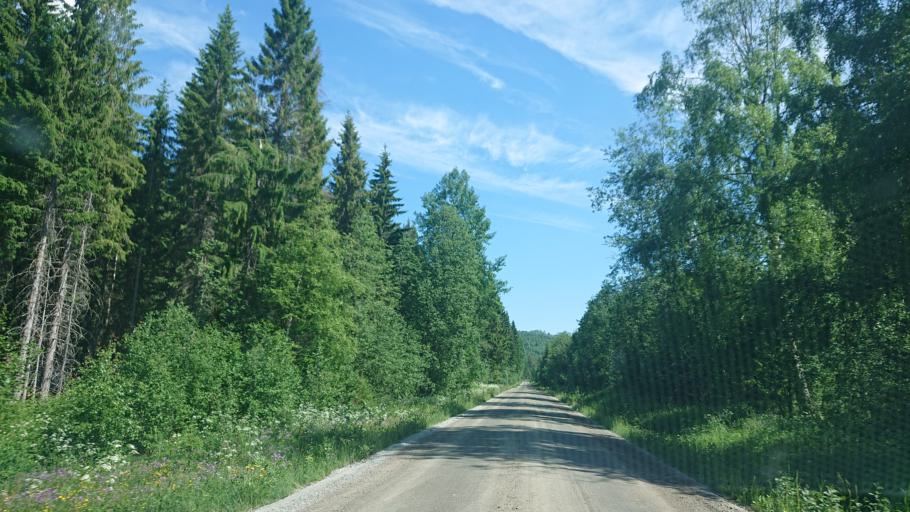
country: SE
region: Vaesternorrland
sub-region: Solleftea Kommun
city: Solleftea
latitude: 62.9705
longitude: 17.1681
